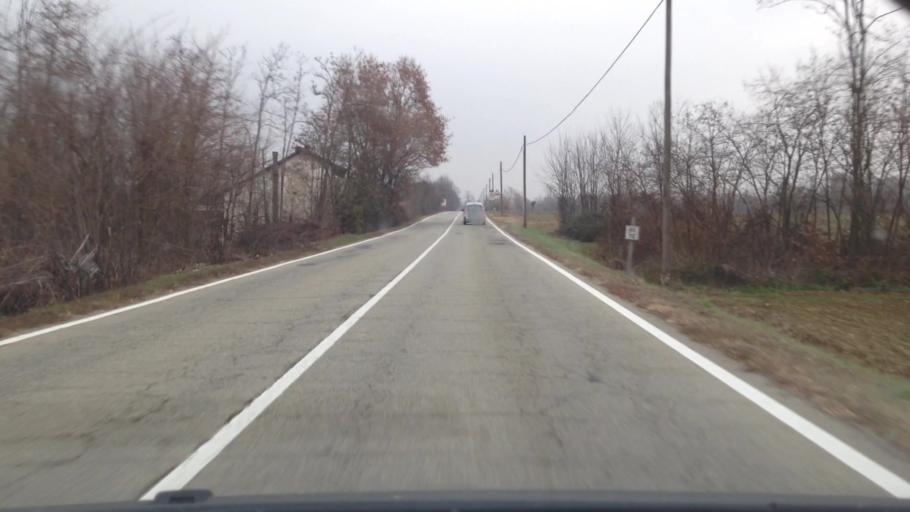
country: IT
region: Piedmont
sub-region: Provincia di Asti
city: Cerro Tanaro
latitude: 44.8872
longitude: 8.3643
